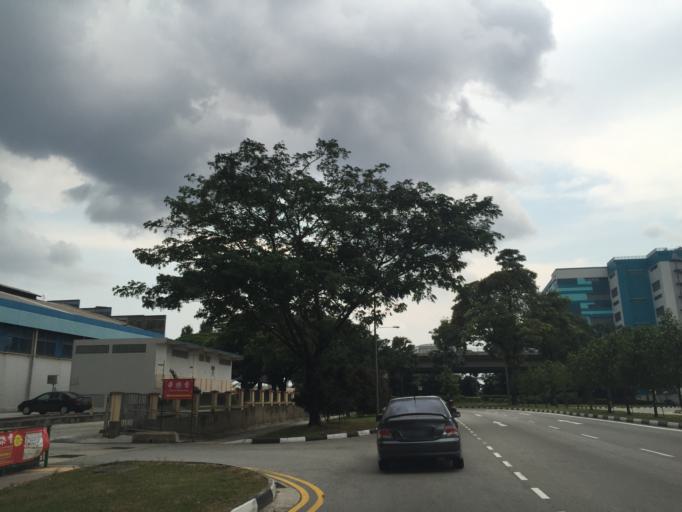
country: MY
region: Johor
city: Johor Bahru
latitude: 1.3241
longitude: 103.6966
